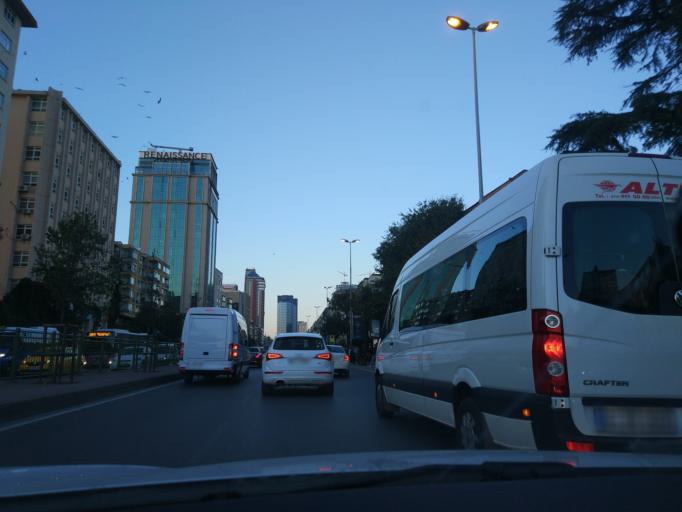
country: TR
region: Istanbul
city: Sisli
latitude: 41.0576
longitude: 29.0102
